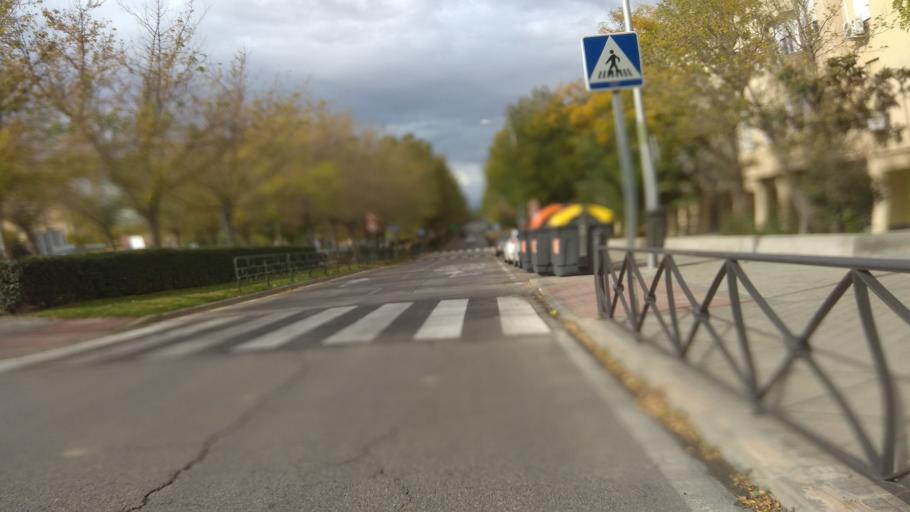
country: ES
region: Madrid
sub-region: Provincia de Madrid
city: Vicalvaro
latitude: 40.4064
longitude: -3.6025
